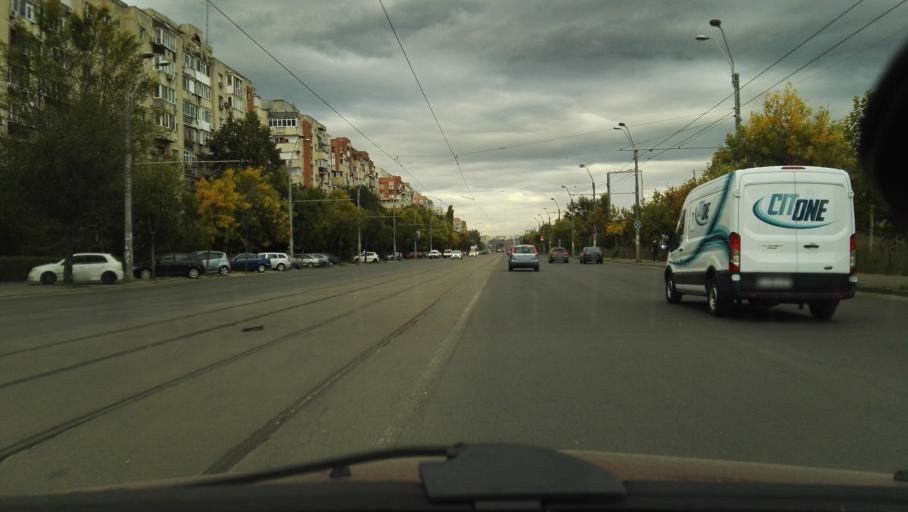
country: RO
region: Bucuresti
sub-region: Municipiul Bucuresti
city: Bucharest
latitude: 44.4007
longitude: 26.1210
